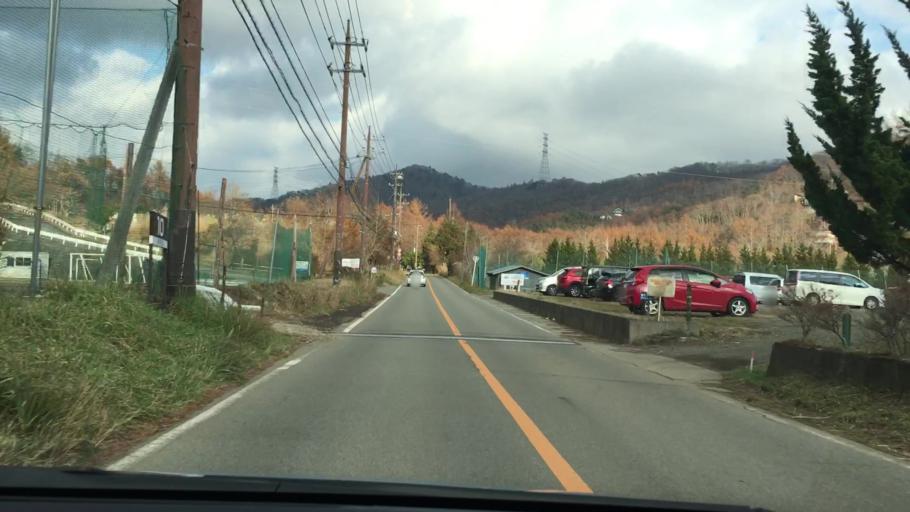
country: JP
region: Shizuoka
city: Gotemba
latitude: 35.4380
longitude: 138.9177
